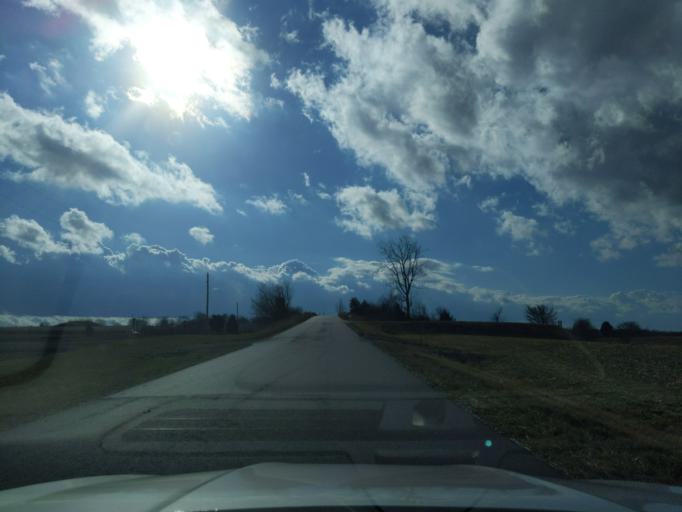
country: US
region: Indiana
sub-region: Decatur County
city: Greensburg
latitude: 39.3643
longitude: -85.4986
